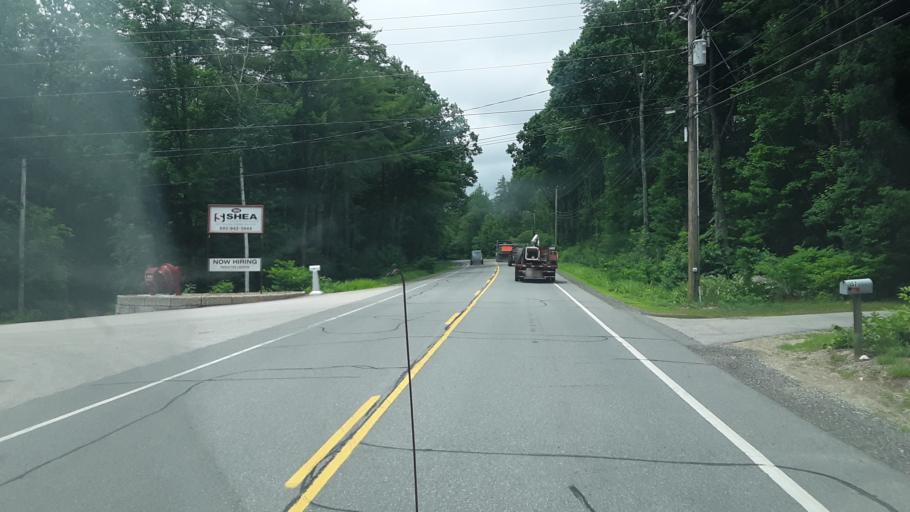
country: US
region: New Hampshire
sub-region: Rockingham County
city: Northwood
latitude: 43.1790
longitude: -71.1048
